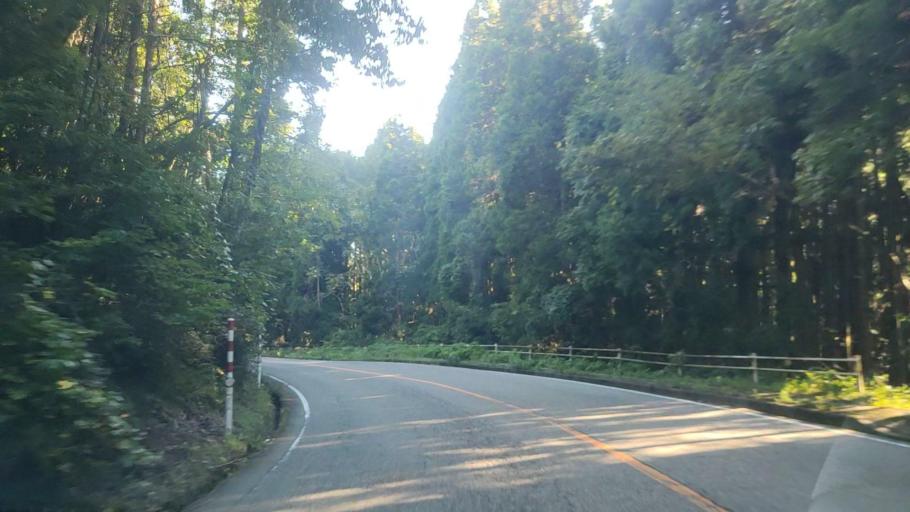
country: JP
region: Ishikawa
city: Nanao
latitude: 37.1017
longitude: 136.9486
